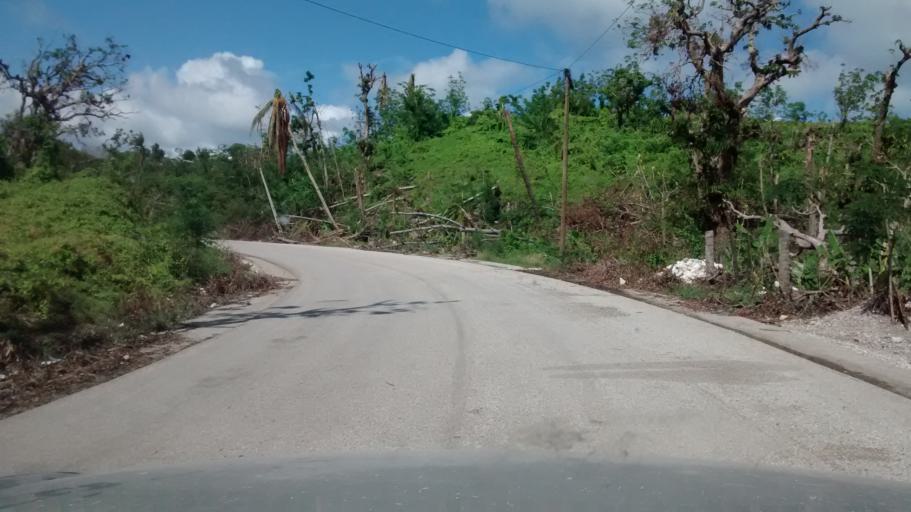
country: HT
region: Grandans
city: Jeremie
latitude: 18.6134
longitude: -74.0822
